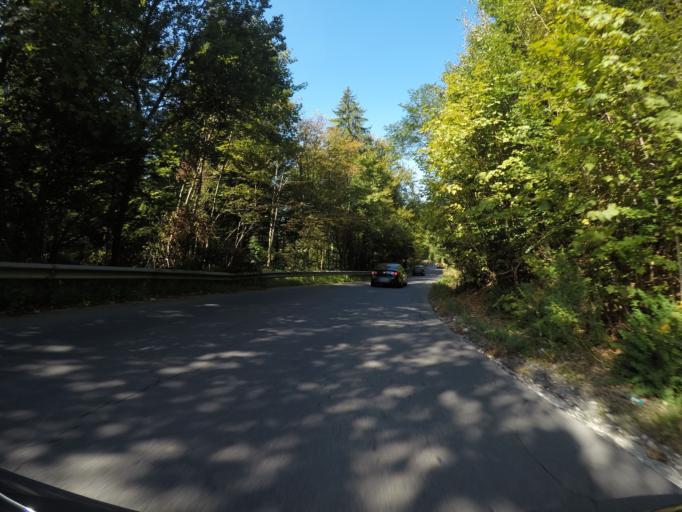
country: RO
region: Brasov
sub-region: Comuna Cristian
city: Cristian
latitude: 45.5940
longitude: 25.5360
